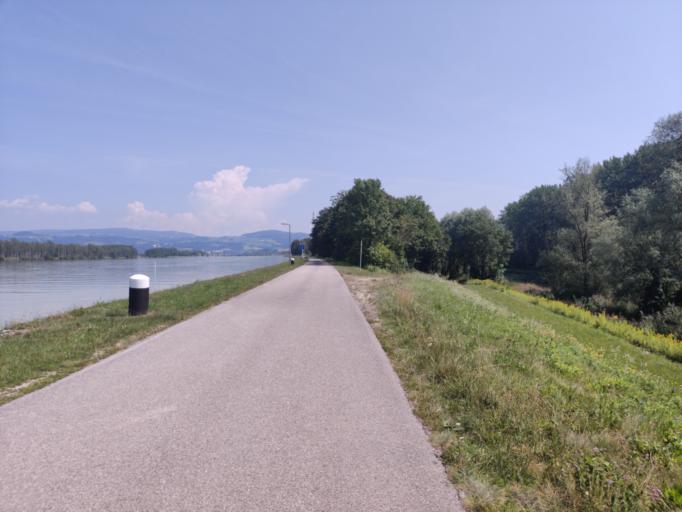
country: AT
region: Upper Austria
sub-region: Politischer Bezirk Urfahr-Umgebung
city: Goldworth
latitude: 48.3089
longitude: 14.1256
